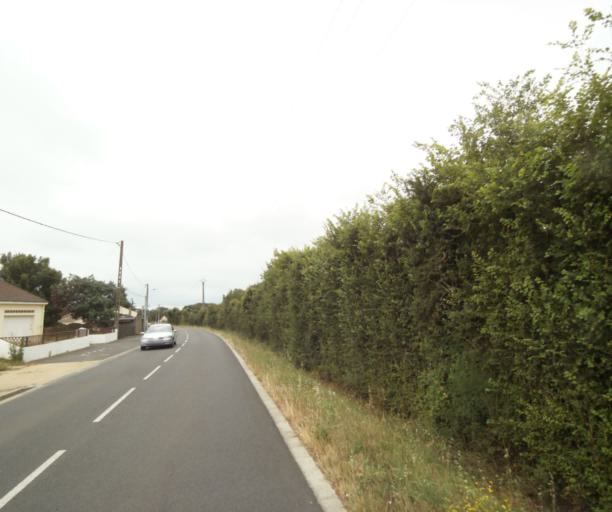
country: FR
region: Pays de la Loire
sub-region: Departement de la Vendee
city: Chateau-d'Olonne
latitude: 46.5113
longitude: -1.7393
